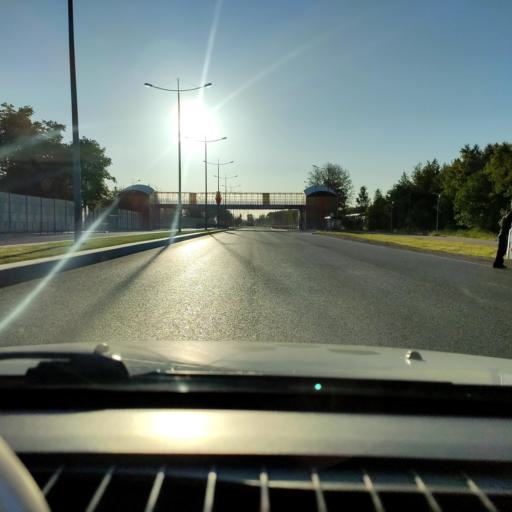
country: RU
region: Perm
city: Kondratovo
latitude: 57.9412
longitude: 56.0614
